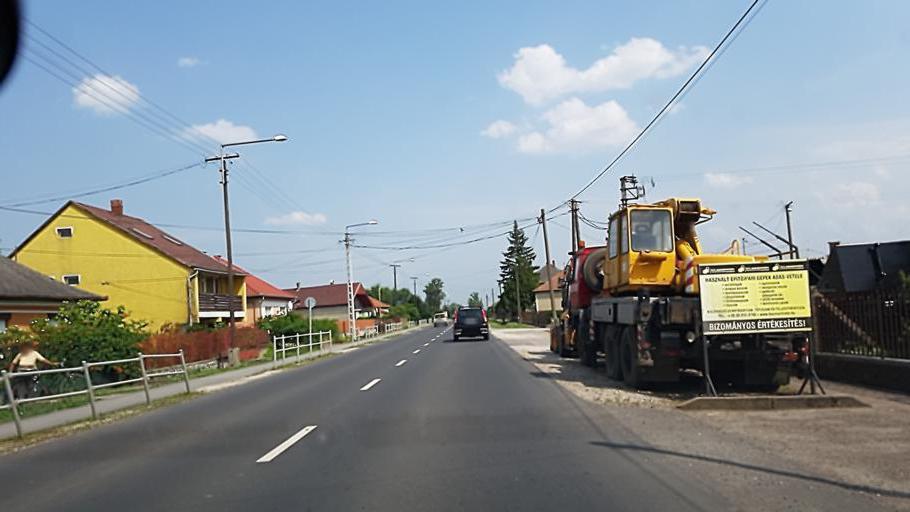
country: HU
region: Heves
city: Besenyotelek
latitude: 47.6937
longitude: 20.4395
